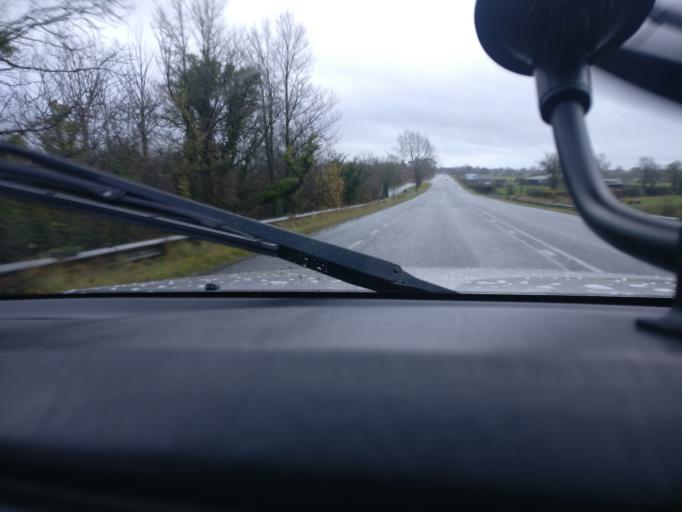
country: IE
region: Leinster
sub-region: An Mhi
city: Longwood
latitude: 53.4287
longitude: -6.9144
